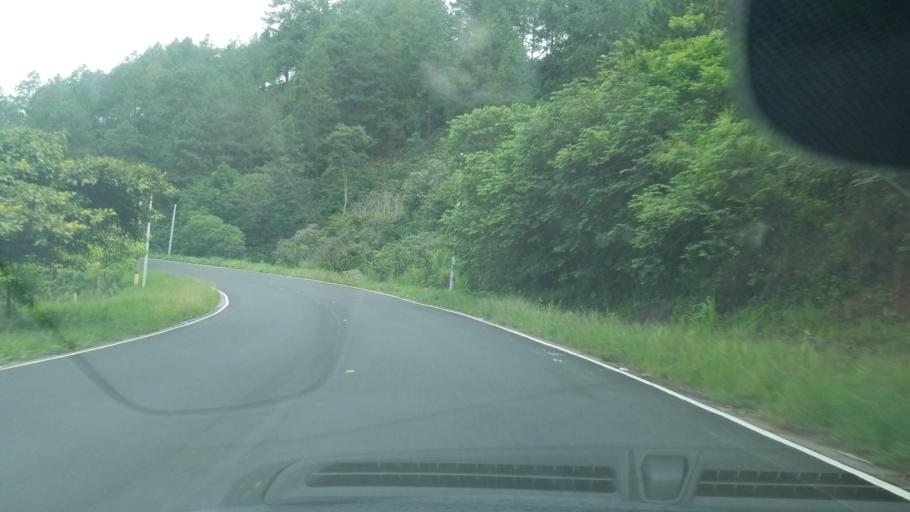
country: HN
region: Ocotepeque
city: Sinuapa
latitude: 14.4562
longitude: -89.1453
